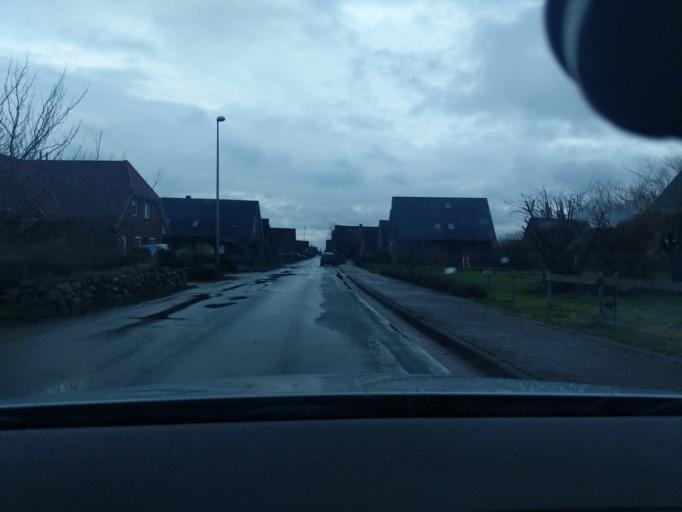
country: DE
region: Lower Saxony
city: Jork
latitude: 53.5228
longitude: 9.6533
